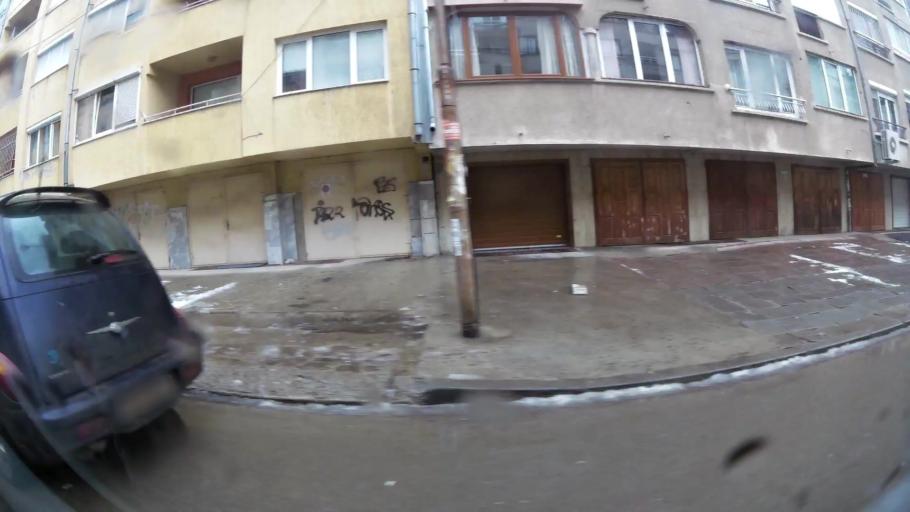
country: BG
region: Sofia-Capital
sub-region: Stolichna Obshtina
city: Sofia
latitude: 42.6699
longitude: 23.2887
